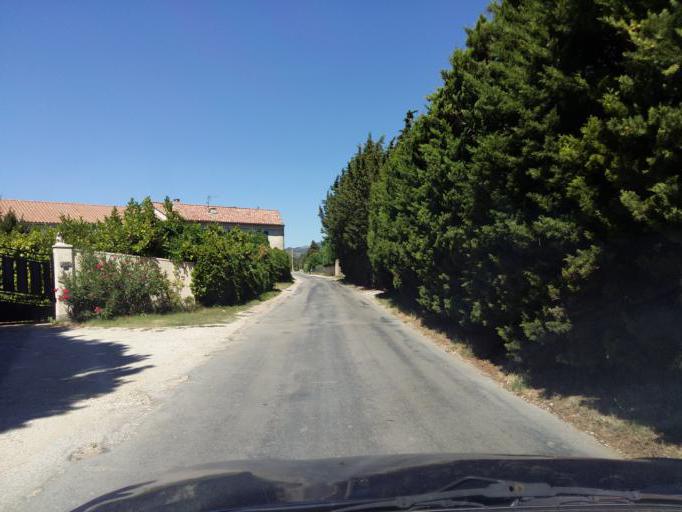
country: FR
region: Provence-Alpes-Cote d'Azur
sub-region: Departement du Vaucluse
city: Loriol-du-Comtat
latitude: 44.0814
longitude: 5.0053
